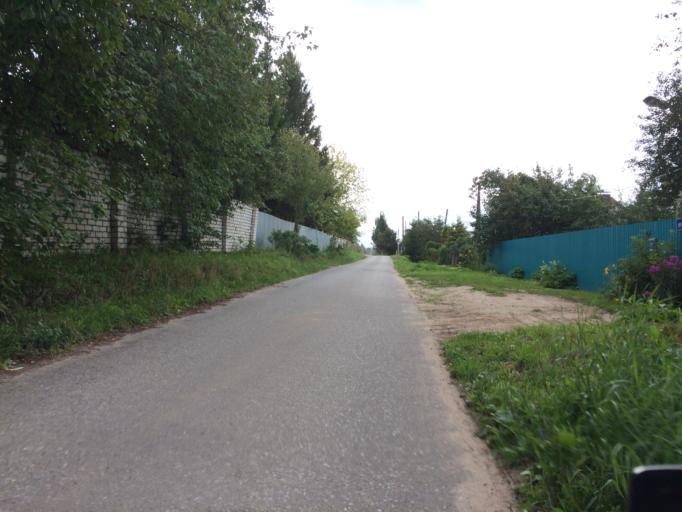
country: RU
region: Mariy-El
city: Yoshkar-Ola
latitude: 56.6647
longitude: 47.9971
